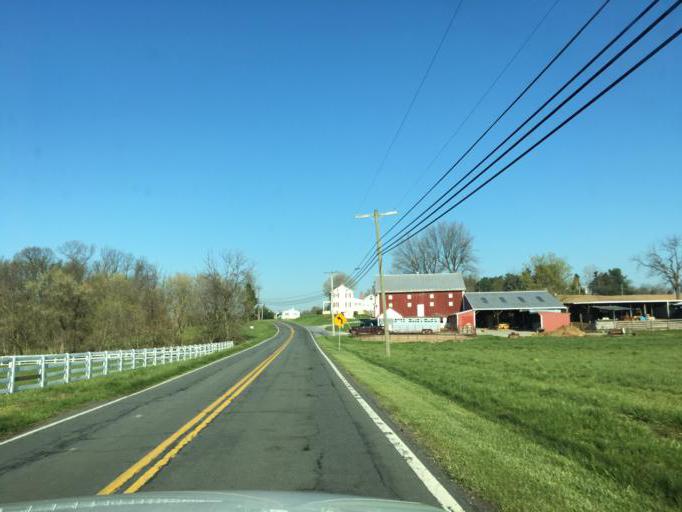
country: US
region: Maryland
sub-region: Frederick County
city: Woodsboro
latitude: 39.4874
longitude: -77.2806
